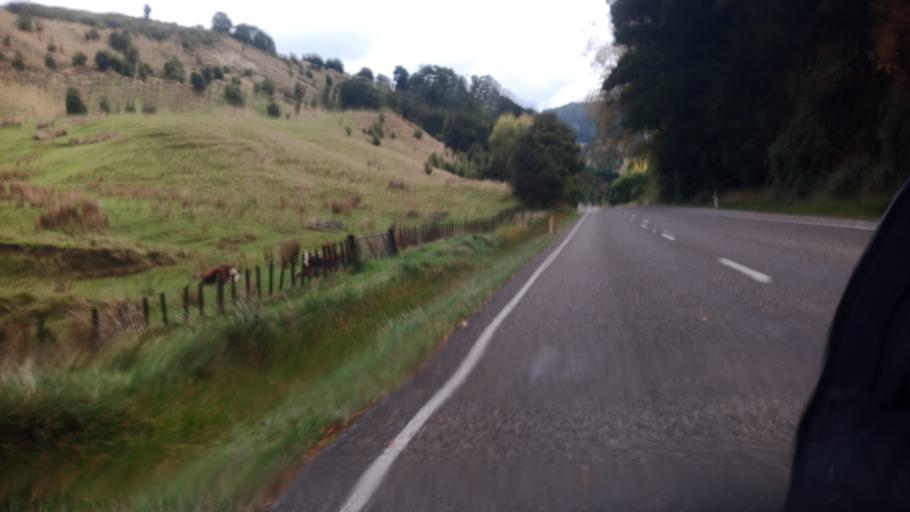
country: NZ
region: Gisborne
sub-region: Gisborne District
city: Gisborne
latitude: -38.2398
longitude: 178.2546
